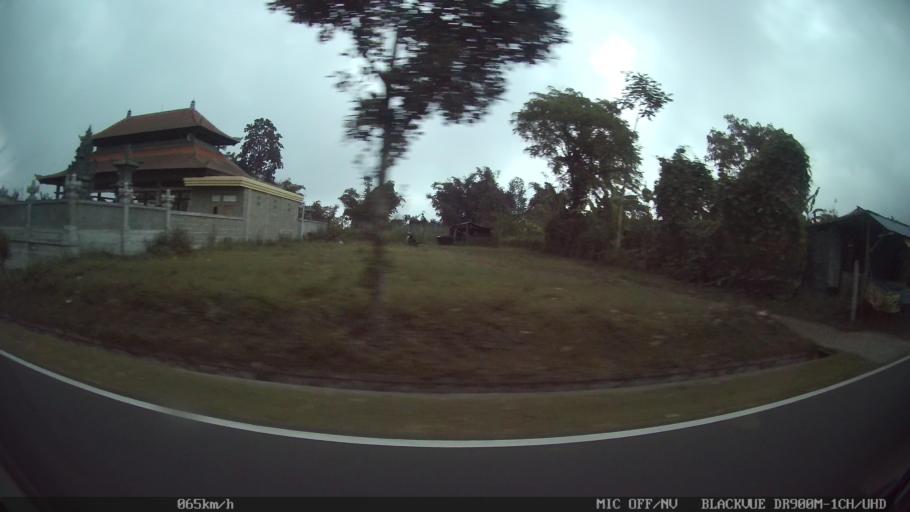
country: ID
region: Bali
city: Banjar Kedisan
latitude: -8.2814
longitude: 115.3219
